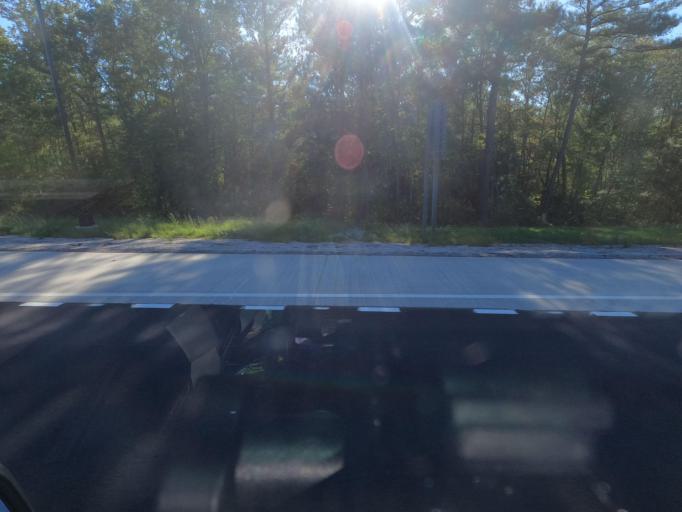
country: US
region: Tennessee
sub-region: Coffee County
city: Manchester
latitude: 35.4231
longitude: -86.0225
